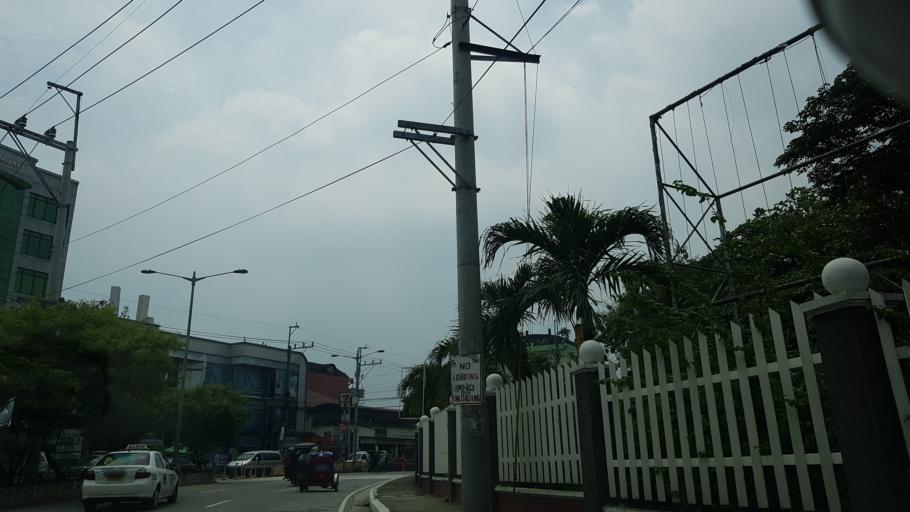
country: PH
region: Metro Manila
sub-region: Makati City
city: Makati City
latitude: 14.5251
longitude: 121.0442
